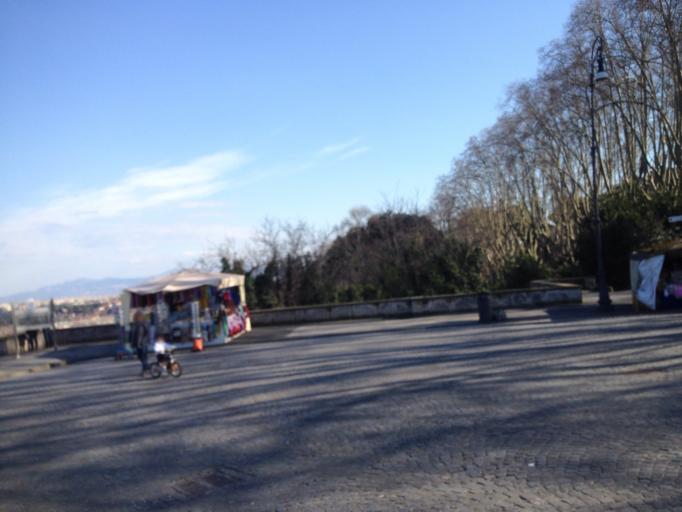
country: VA
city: Vatican City
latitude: 41.8913
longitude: 12.4613
